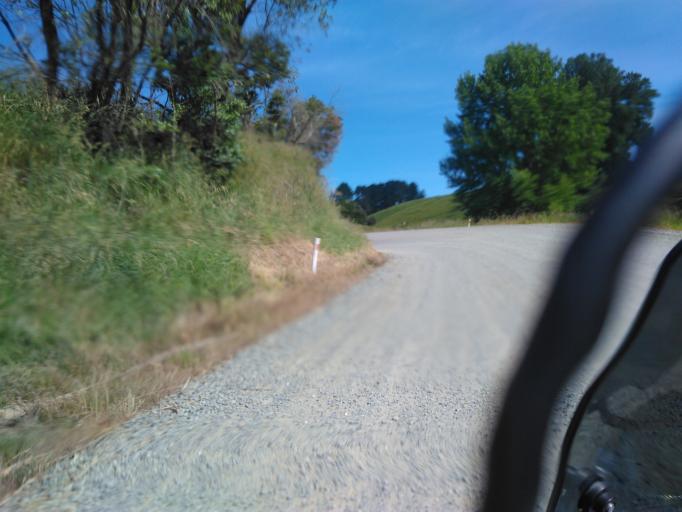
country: NZ
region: Hawke's Bay
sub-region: Wairoa District
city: Wairoa
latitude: -38.8708
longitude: 177.2079
